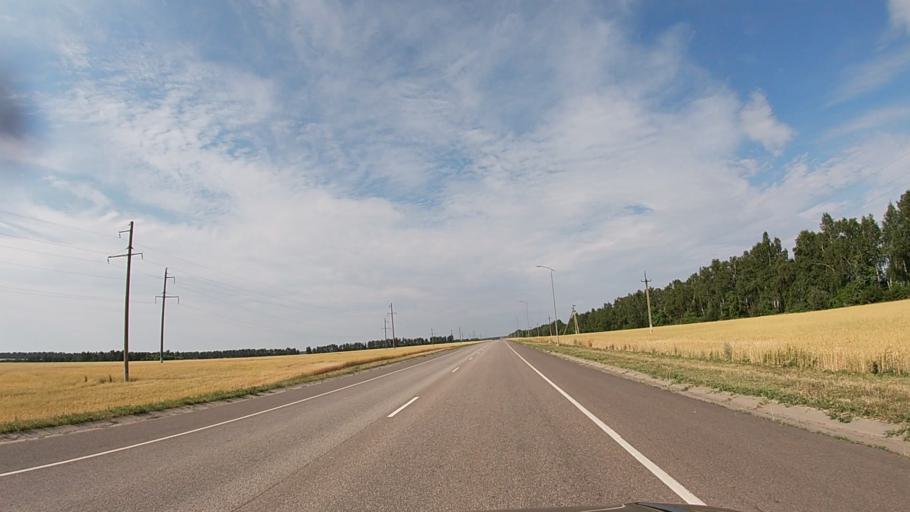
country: RU
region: Belgorod
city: Proletarskiy
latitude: 50.8282
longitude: 35.7621
